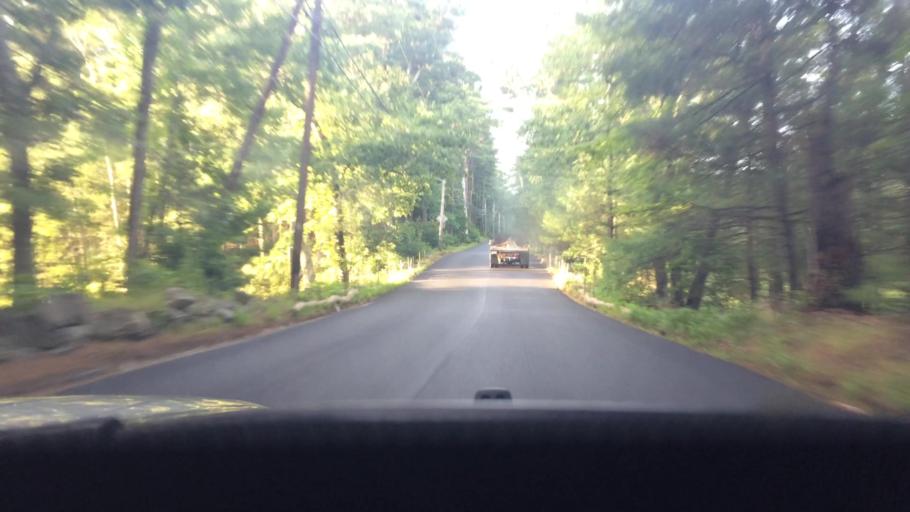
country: US
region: Massachusetts
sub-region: Middlesex County
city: North Reading
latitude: 42.6185
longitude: -71.0935
